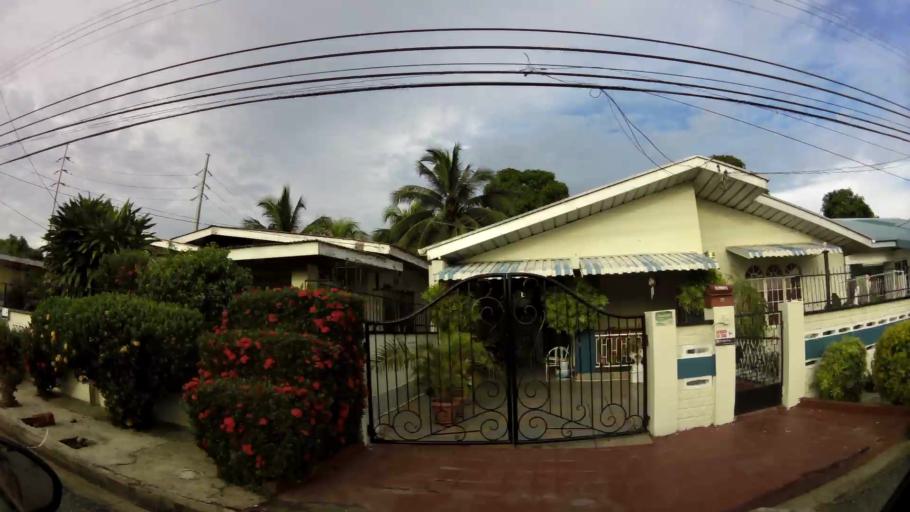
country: TT
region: Tunapuna/Piarco
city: Tunapuna
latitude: 10.6420
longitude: -61.4112
